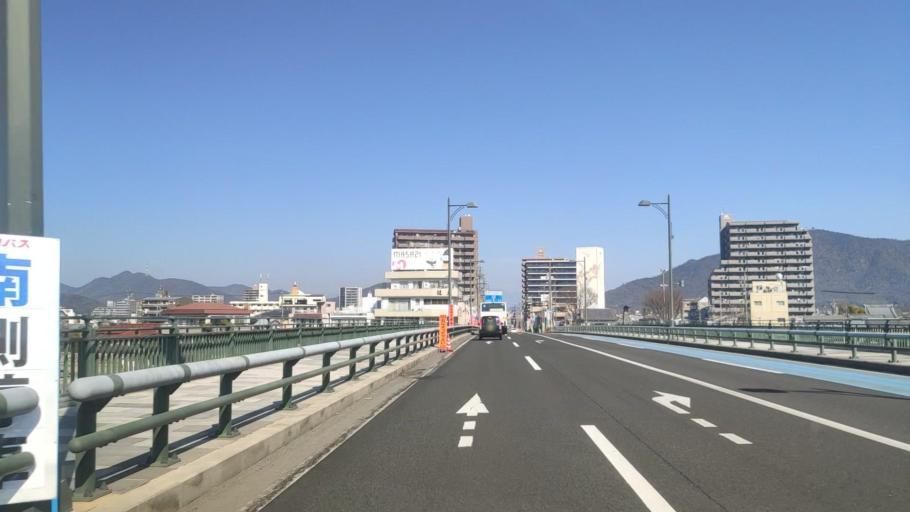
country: JP
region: Gifu
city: Gifu-shi
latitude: 35.4396
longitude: 136.7734
